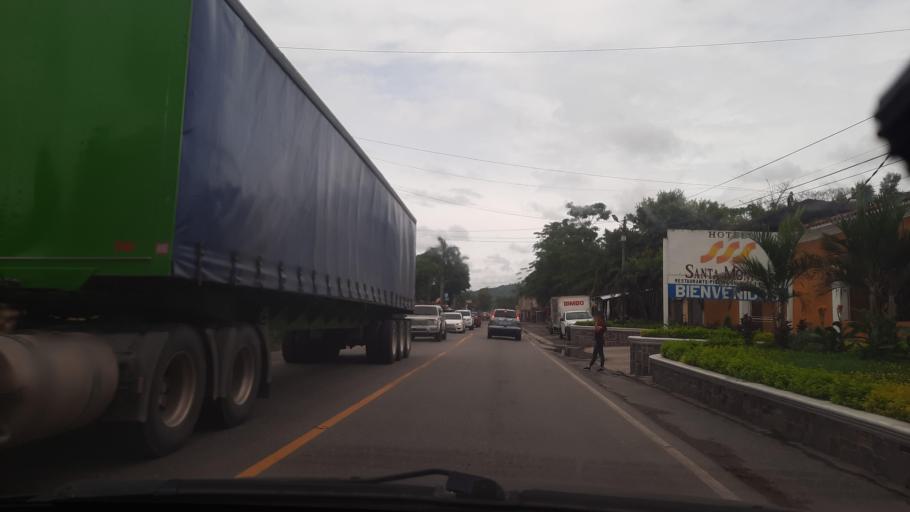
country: GT
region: Izabal
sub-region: Municipio de Los Amates
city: Los Amates
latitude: 15.2545
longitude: -89.0997
